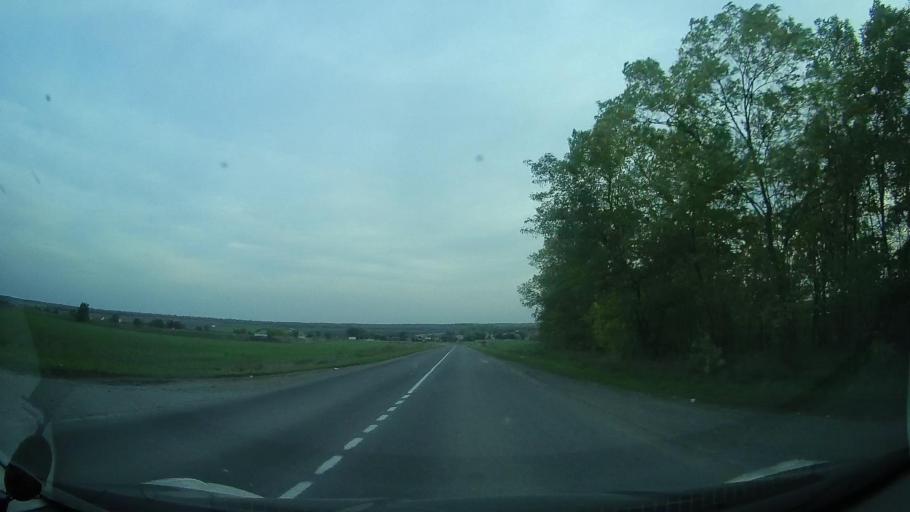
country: RU
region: Rostov
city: Kirovskaya
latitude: 47.0400
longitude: 39.9777
